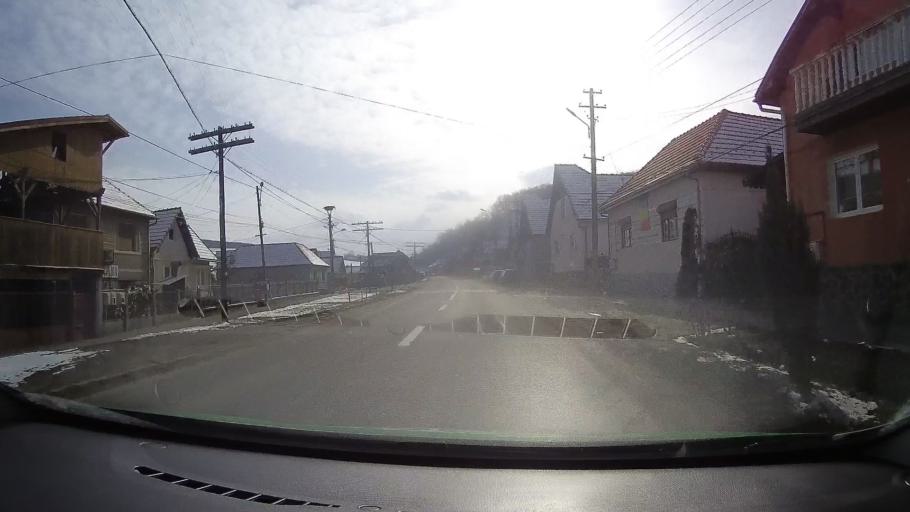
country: RO
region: Mures
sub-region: Municipiul Sighisoara
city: Sighisoara
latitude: 46.2095
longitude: 24.7792
